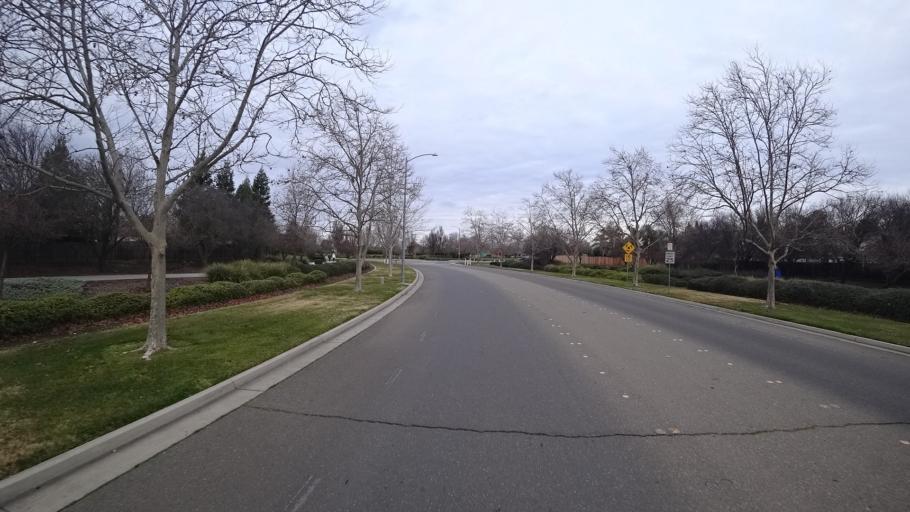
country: US
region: California
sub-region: Yolo County
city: Davis
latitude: 38.5642
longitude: -121.7179
